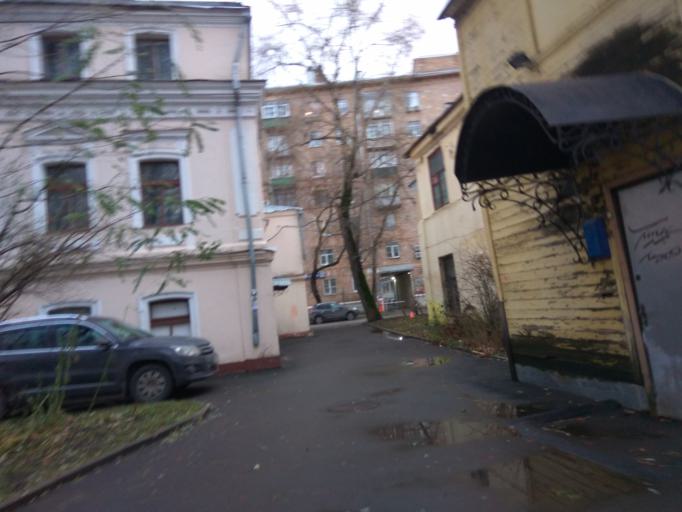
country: RU
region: Moscow
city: Taganskiy
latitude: 55.7443
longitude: 37.6621
